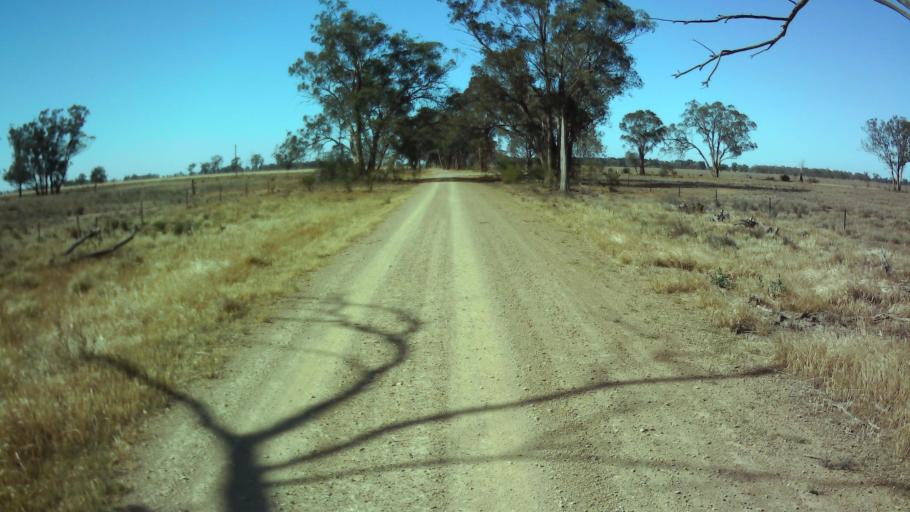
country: AU
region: New South Wales
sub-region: Weddin
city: Grenfell
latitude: -33.9438
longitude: 147.8704
